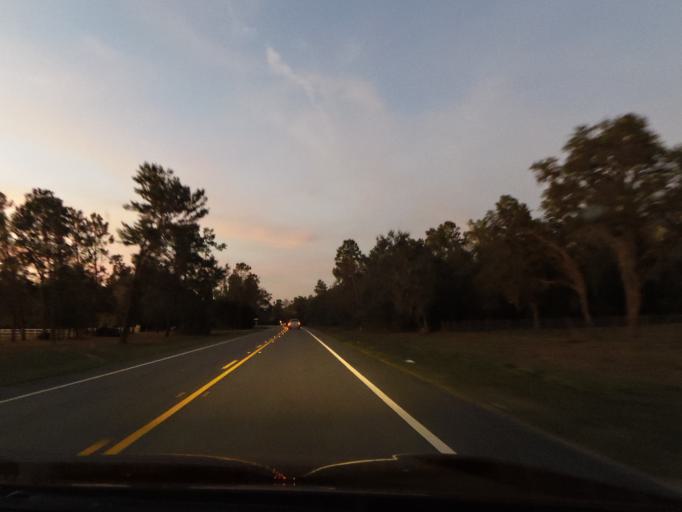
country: US
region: Florida
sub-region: Volusia County
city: De Leon Springs
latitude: 29.2140
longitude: -81.3156
